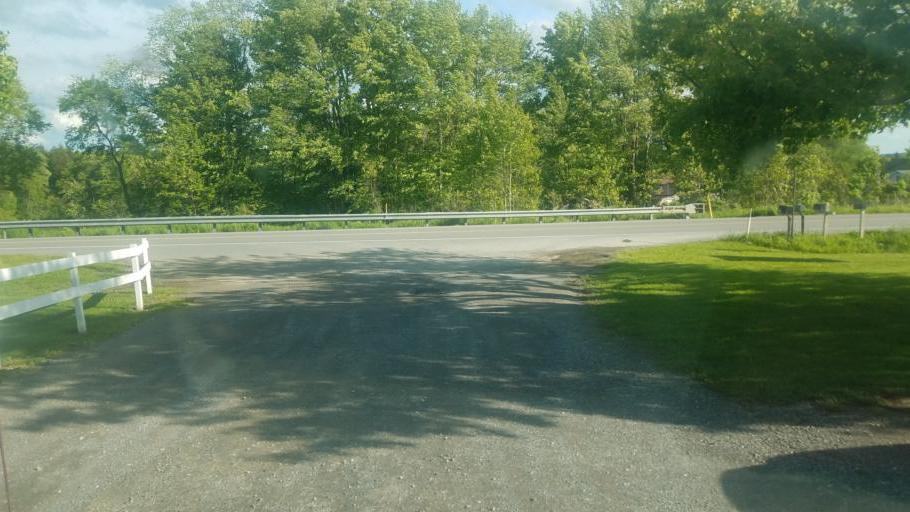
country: US
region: Pennsylvania
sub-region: McKean County
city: Kane
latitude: 41.6737
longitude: -78.7635
